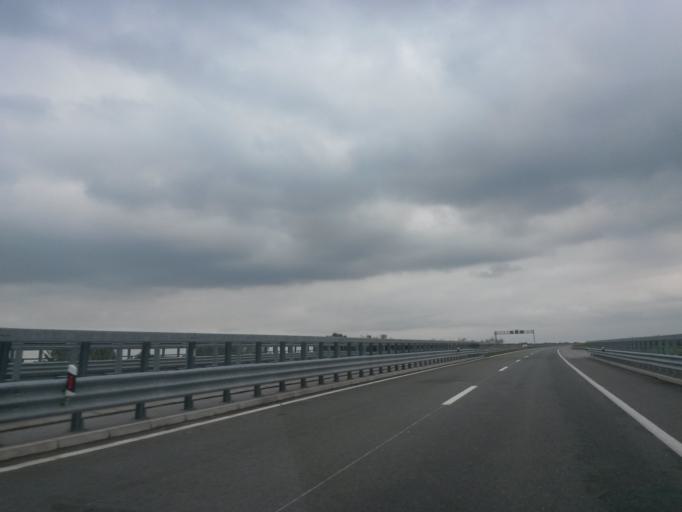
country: HR
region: Osjecko-Baranjska
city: Gorjani
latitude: 45.3656
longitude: 18.3970
